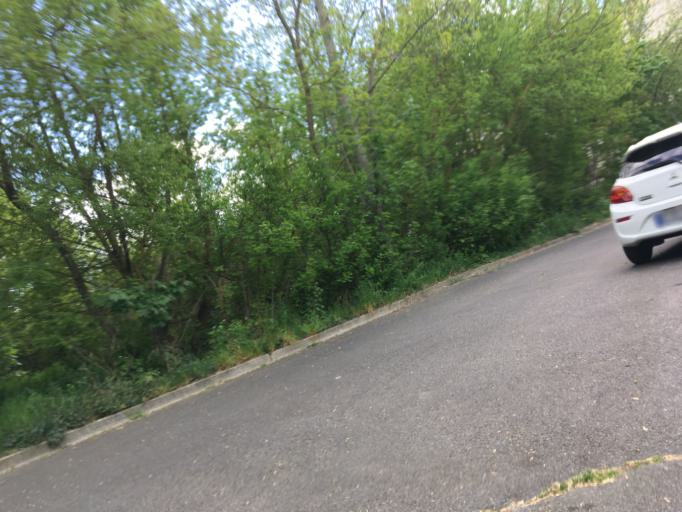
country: DE
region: Berlin
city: Hellersdorf
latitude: 52.5379
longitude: 13.6245
